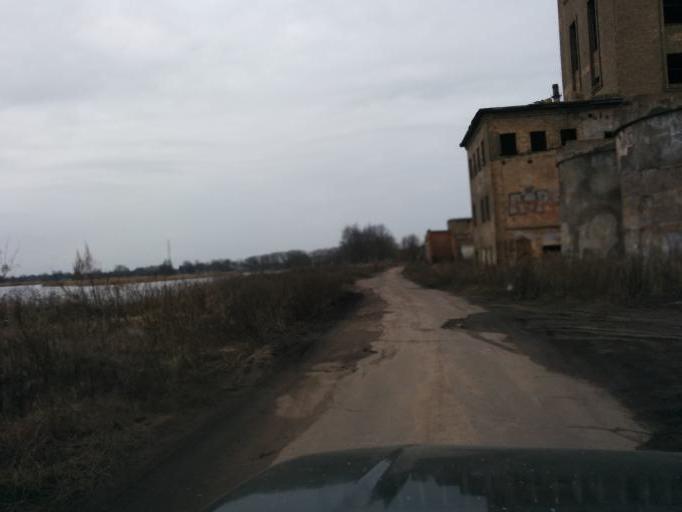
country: LV
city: Tireli
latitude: 56.9420
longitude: 23.6369
